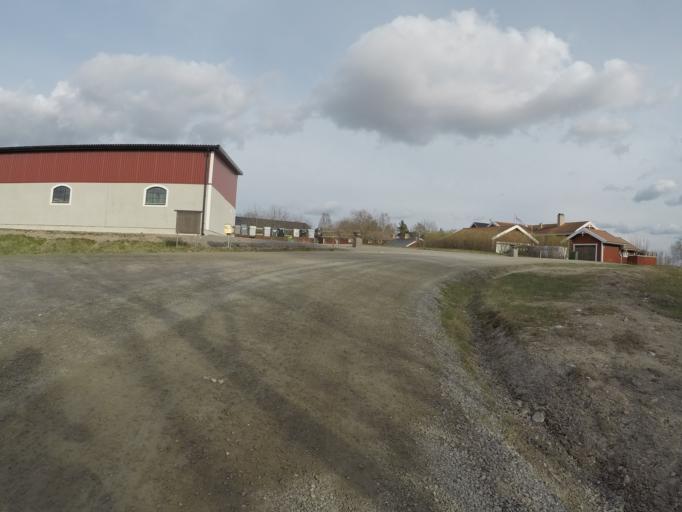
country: SE
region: Soedermanland
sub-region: Eskilstuna Kommun
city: Eskilstuna
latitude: 59.4388
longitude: 16.5640
